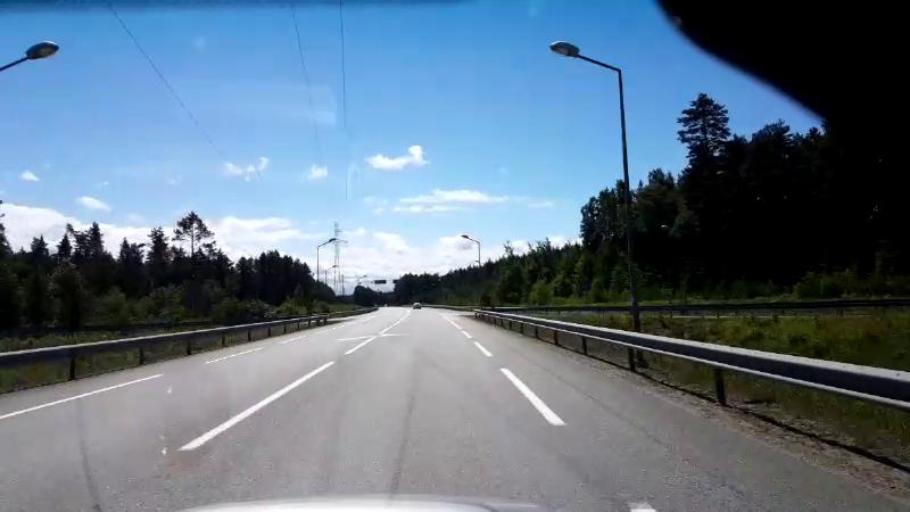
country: LV
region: Saulkrastu
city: Saulkrasti
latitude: 57.2409
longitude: 24.4268
